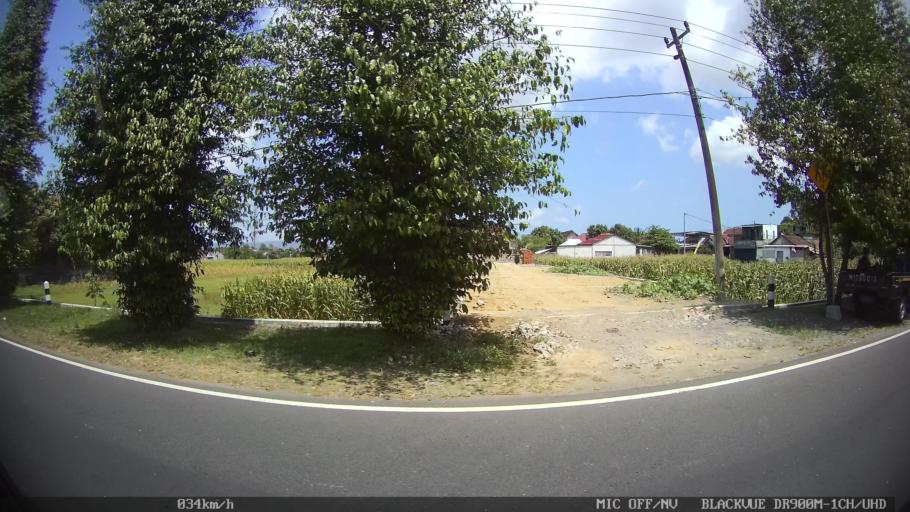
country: ID
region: Daerah Istimewa Yogyakarta
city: Sewon
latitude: -7.8827
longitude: 110.3445
